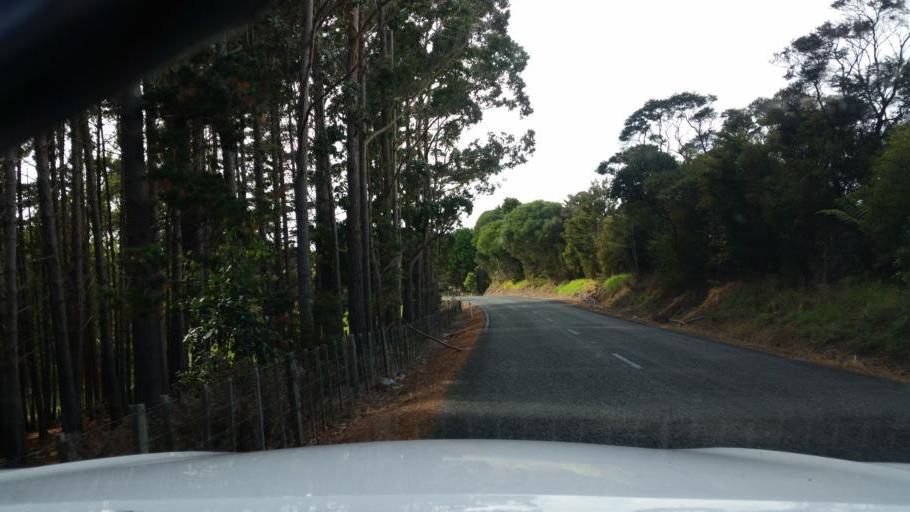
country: NZ
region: Auckland
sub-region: Auckland
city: Wellsford
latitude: -36.0860
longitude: 174.5492
